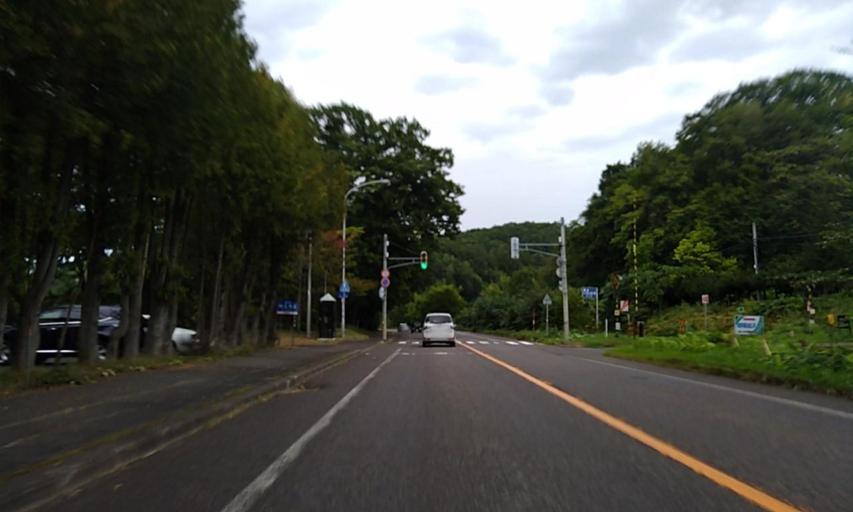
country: JP
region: Hokkaido
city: Abashiri
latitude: 43.9827
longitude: 144.2191
